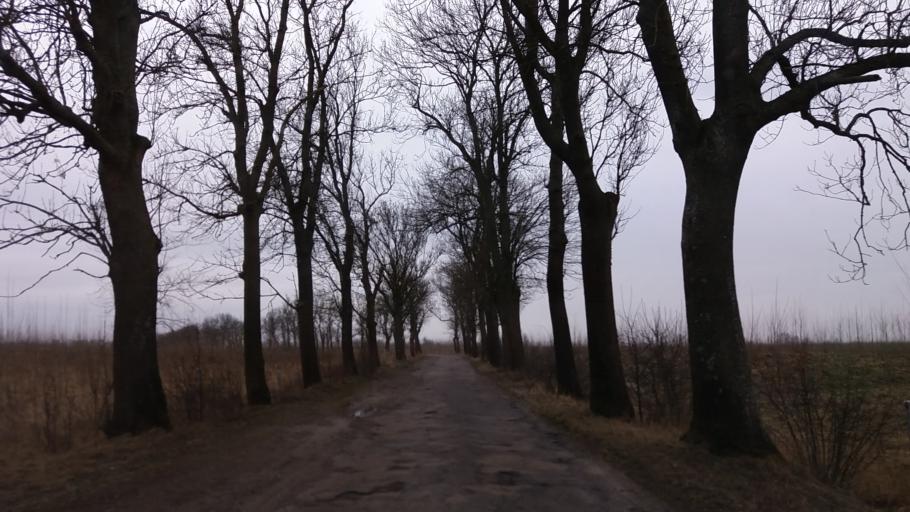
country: PL
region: West Pomeranian Voivodeship
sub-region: Powiat choszczenski
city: Bierzwnik
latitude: 53.0370
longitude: 15.7326
